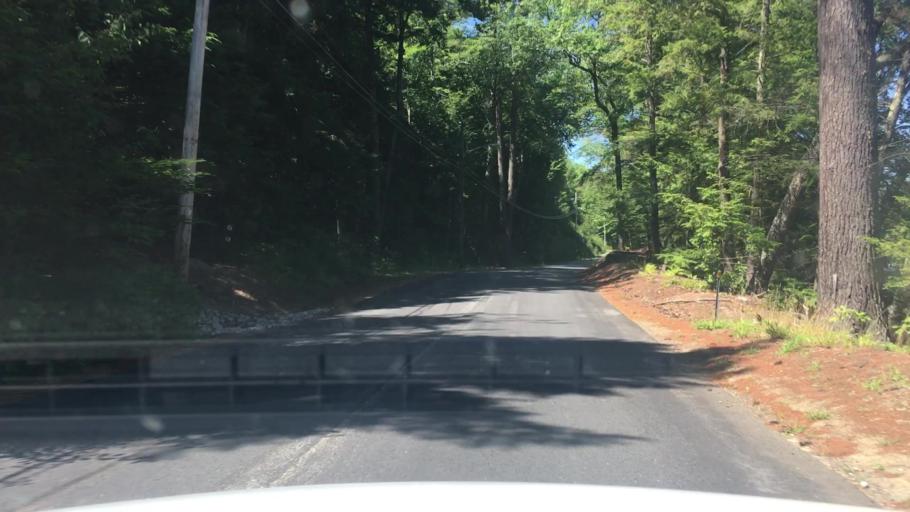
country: US
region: New Hampshire
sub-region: Merrimack County
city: Hopkinton
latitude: 43.2388
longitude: -71.6275
